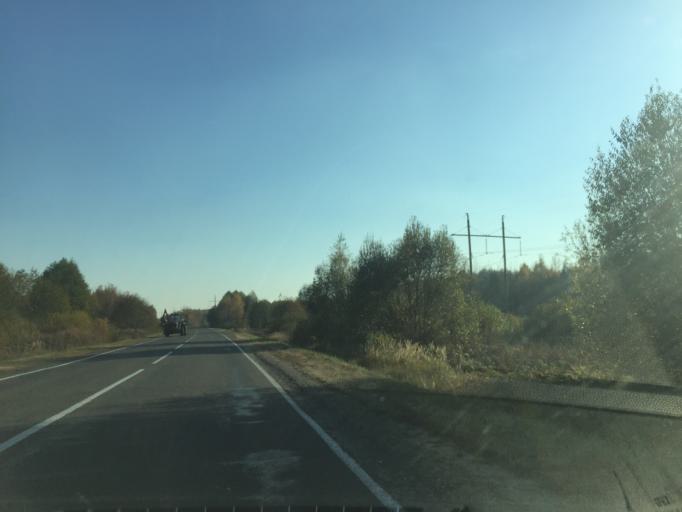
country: BY
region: Gomel
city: Dobrush
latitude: 52.3445
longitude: 31.2304
